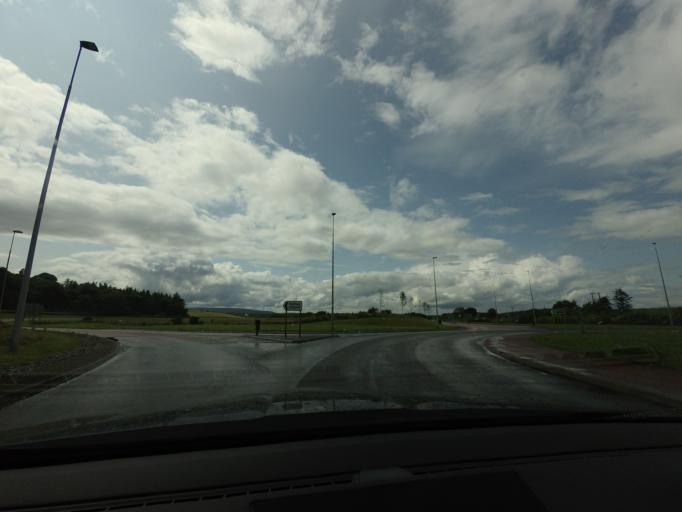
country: GB
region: Scotland
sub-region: Moray
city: Fochabers
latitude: 57.6224
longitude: -3.1149
